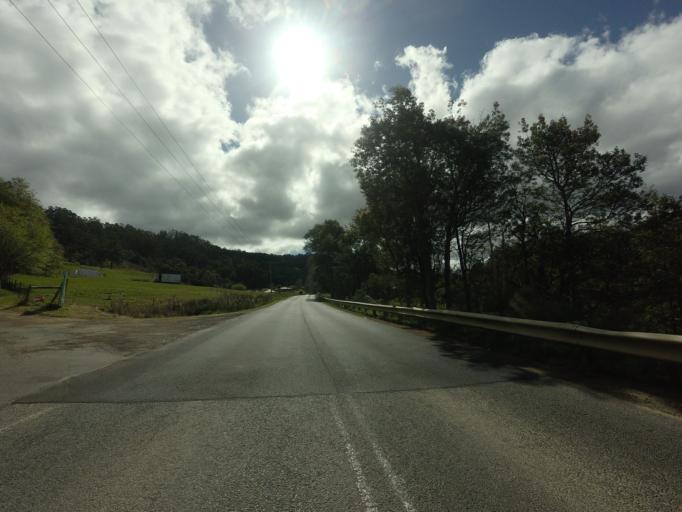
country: AU
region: Tasmania
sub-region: Huon Valley
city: Cygnet
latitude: -43.3057
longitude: 147.0092
